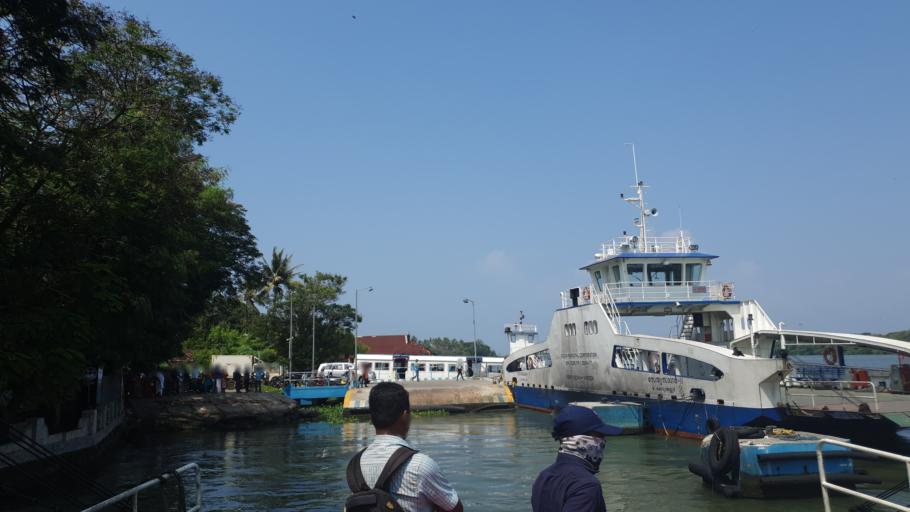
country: IN
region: Kerala
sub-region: Ernakulam
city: Cochin
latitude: 9.9734
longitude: 76.2447
